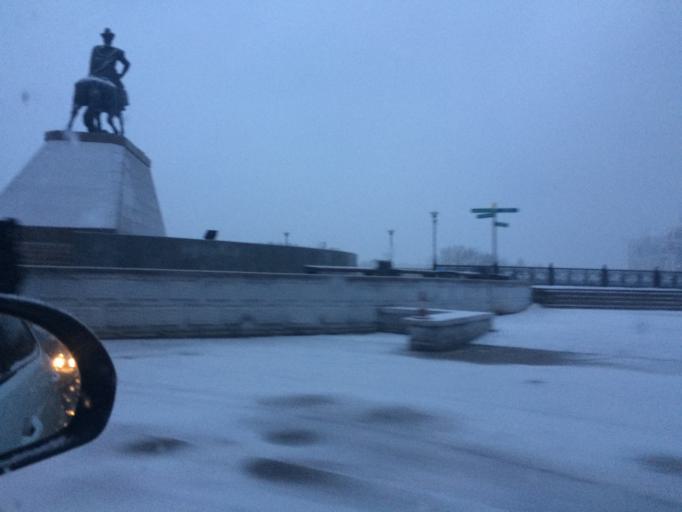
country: KZ
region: Astana Qalasy
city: Astana
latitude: 51.1608
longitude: 71.4242
